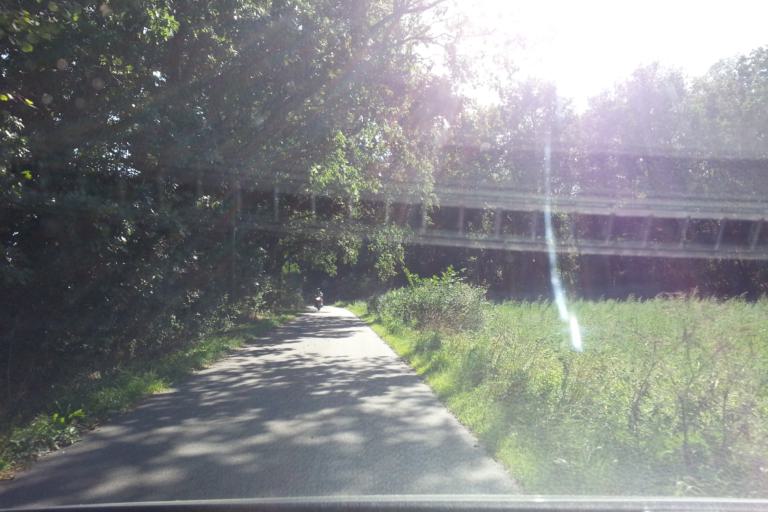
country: DE
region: Mecklenburg-Vorpommern
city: Eggesin
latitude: 53.6935
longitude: 14.0594
